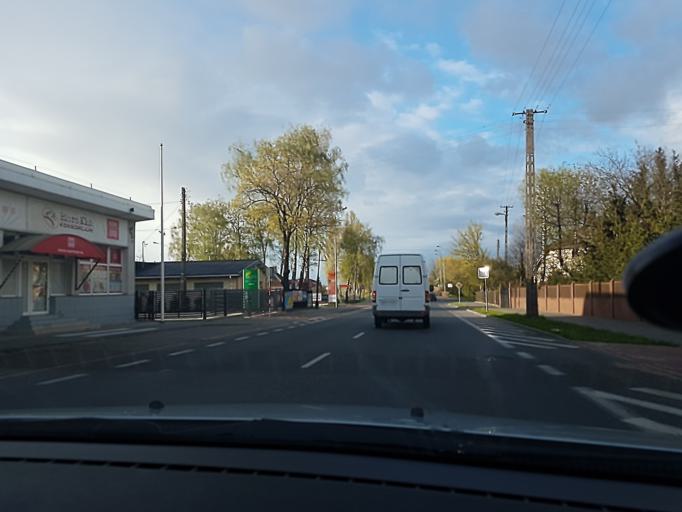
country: PL
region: Lodz Voivodeship
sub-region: Powiat kutnowski
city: Kutno
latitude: 52.2251
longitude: 19.3438
